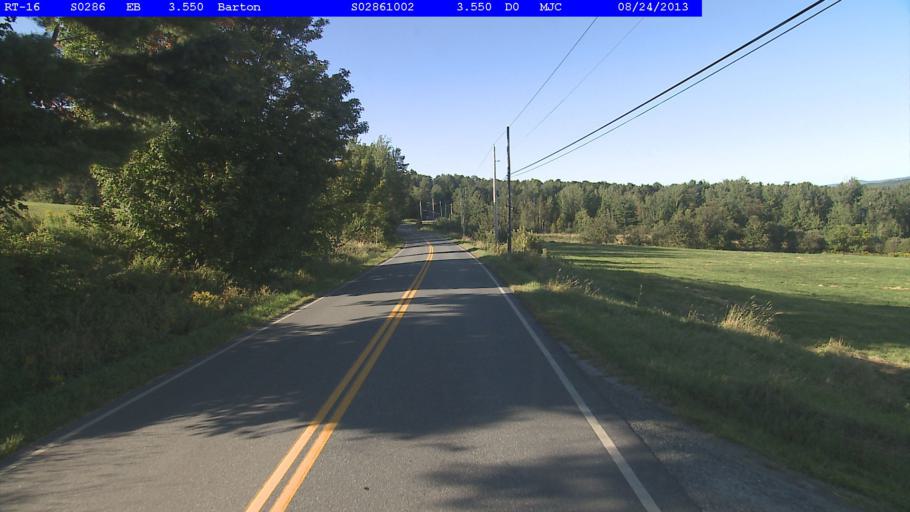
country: US
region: Vermont
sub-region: Orleans County
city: Newport
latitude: 44.7735
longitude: -72.1290
